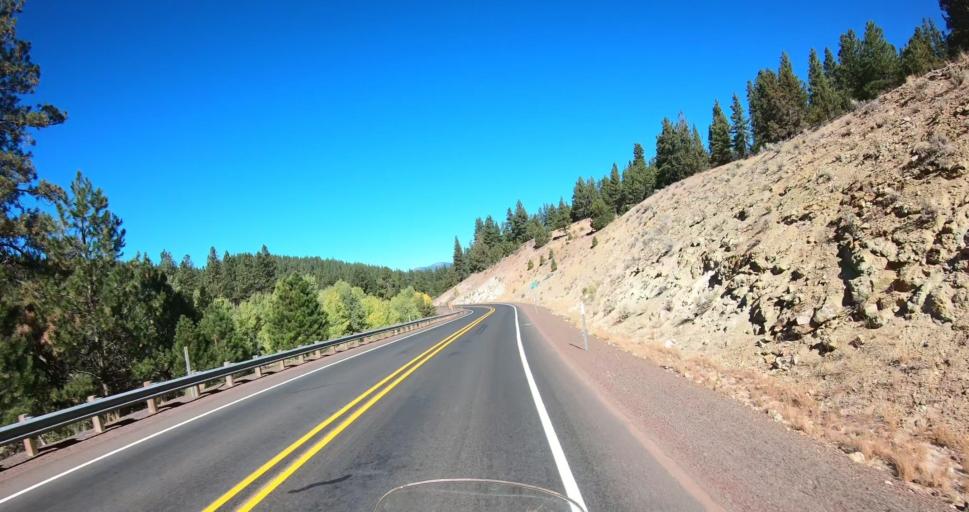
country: US
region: Oregon
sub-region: Lake County
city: Lakeview
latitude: 42.2535
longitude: -120.3298
